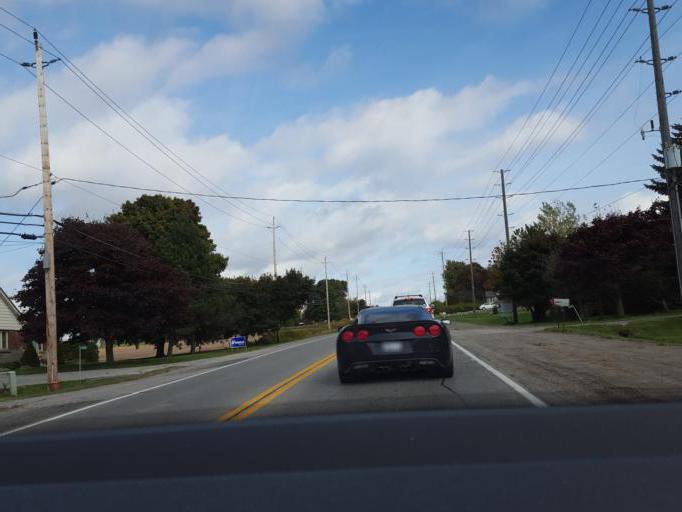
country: CA
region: Ontario
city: Oshawa
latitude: 43.9487
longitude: -78.8093
